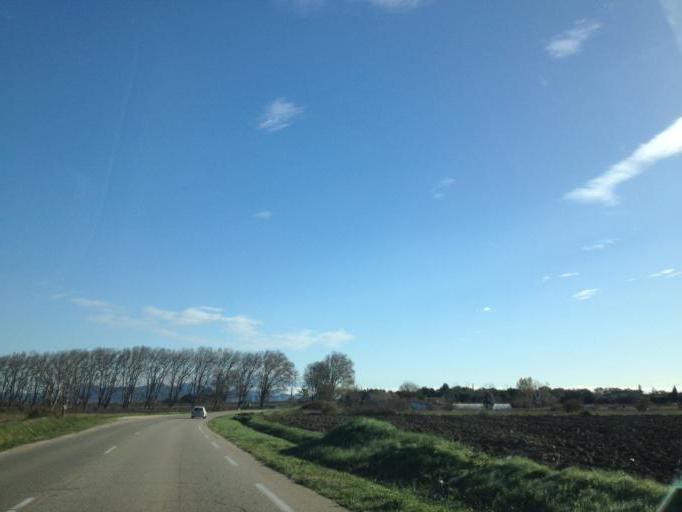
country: FR
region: Provence-Alpes-Cote d'Azur
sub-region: Departement du Vaucluse
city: Courthezon
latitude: 44.1181
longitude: 4.8608
